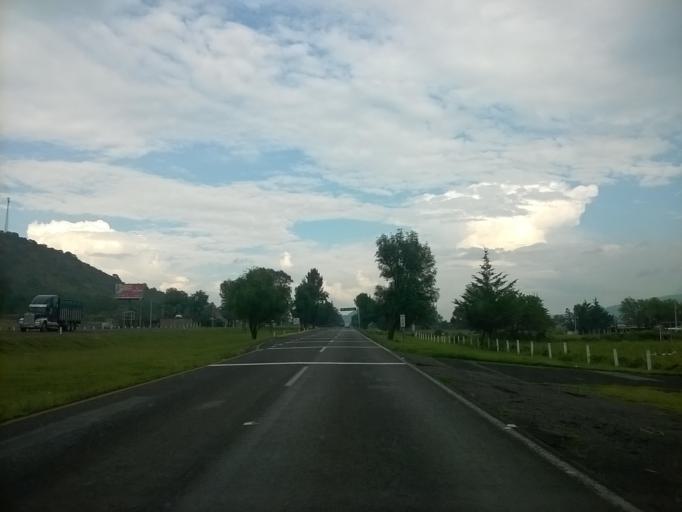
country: MX
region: Michoacan
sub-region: Huiramba
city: El Pedregal
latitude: 19.5318
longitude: -101.4898
